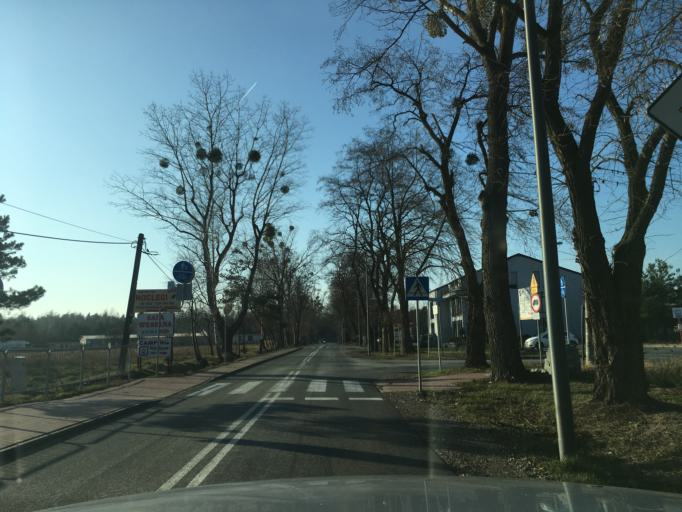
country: PL
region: Lodz Voivodeship
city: Zabia Wola
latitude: 52.0487
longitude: 20.7456
